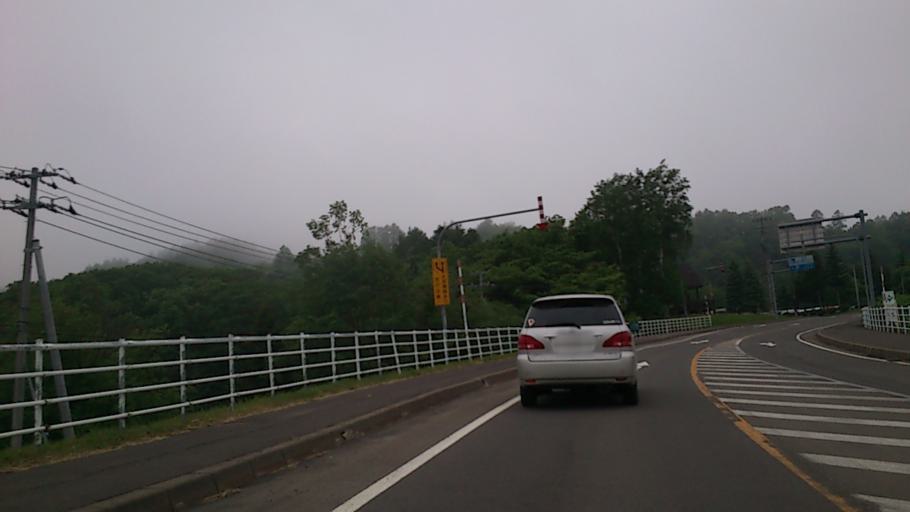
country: JP
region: Hokkaido
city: Niseko Town
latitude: 42.8589
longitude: 140.8725
